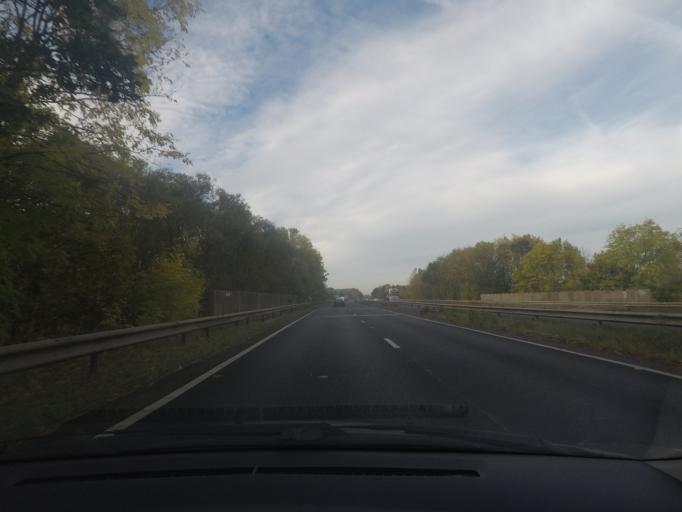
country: GB
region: England
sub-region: City of York
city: Bishopthorpe
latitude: 53.9251
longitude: -1.1117
